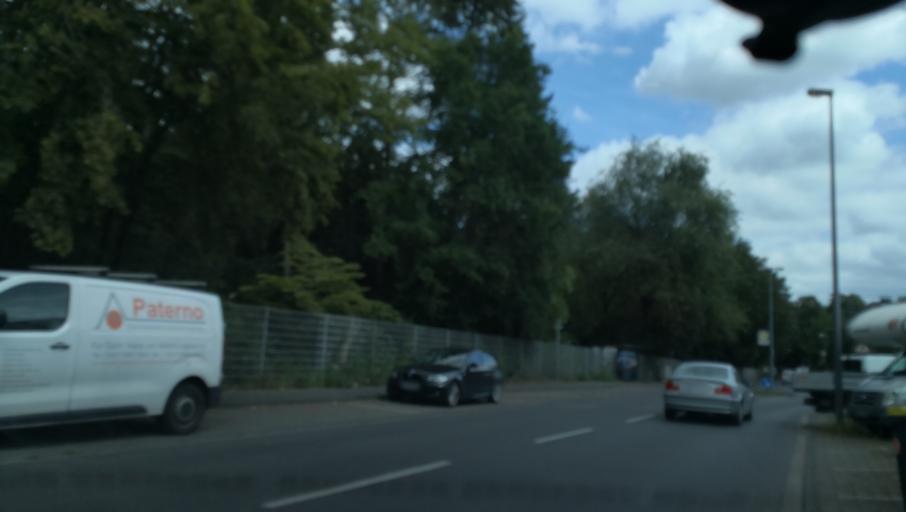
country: DE
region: North Rhine-Westphalia
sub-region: Regierungsbezirk Koln
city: Bilderstoeckchen
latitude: 50.9769
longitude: 6.9350
